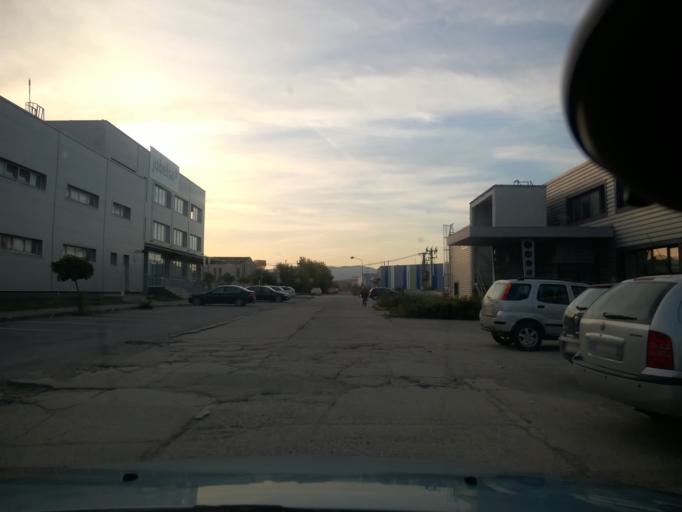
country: SK
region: Kosicky
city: Kosice
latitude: 48.6943
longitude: 21.2494
